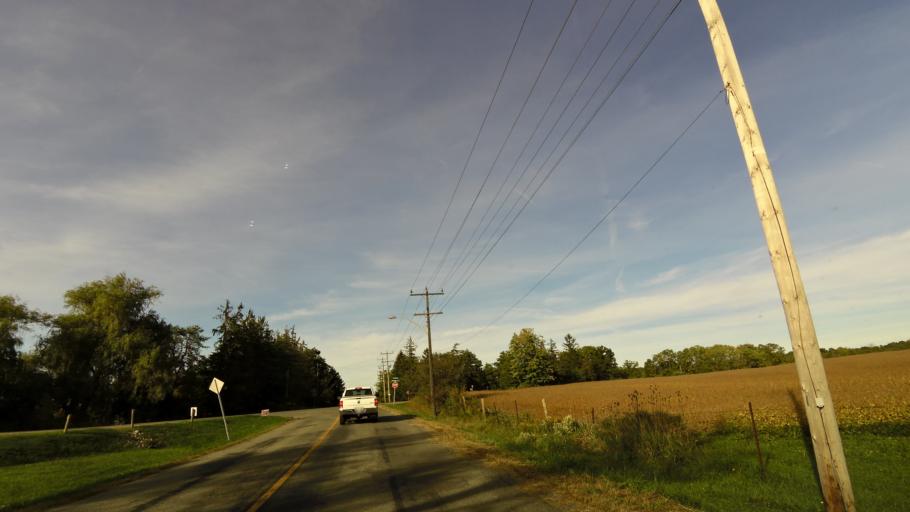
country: CA
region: Ontario
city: Ancaster
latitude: 43.1510
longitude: -79.9537
